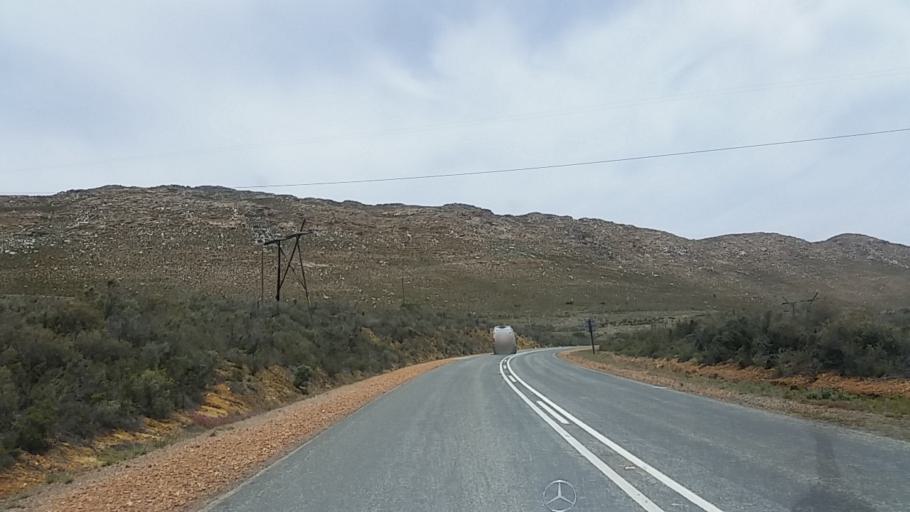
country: ZA
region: Western Cape
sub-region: Eden District Municipality
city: Knysna
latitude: -33.7389
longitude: 23.0390
